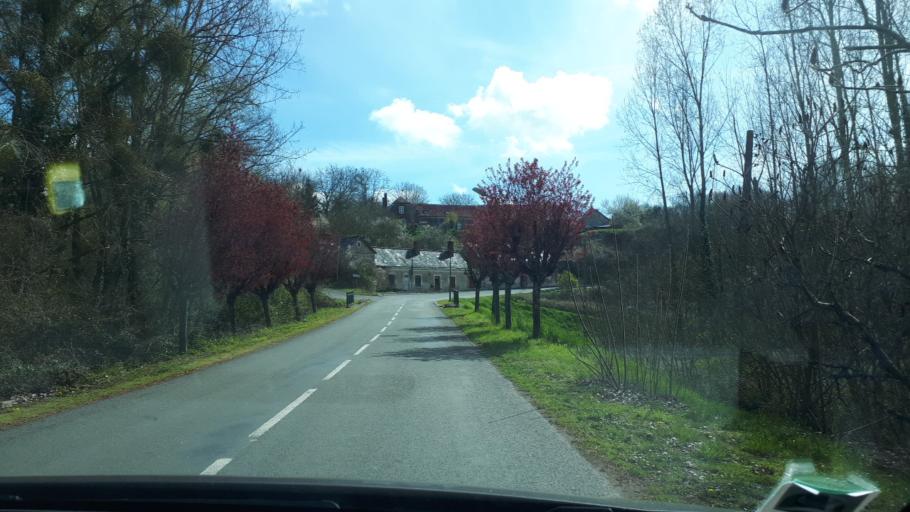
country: FR
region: Pays de la Loire
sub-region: Departement de la Sarthe
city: Bouloire
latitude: 47.9030
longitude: 0.5762
